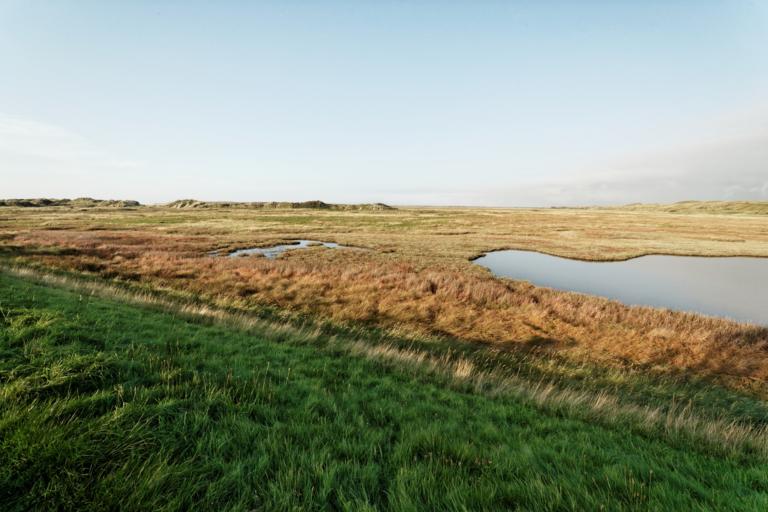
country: NL
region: North Holland
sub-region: Gemeente Texel
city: Den Burg
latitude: 53.1290
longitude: 4.8095
